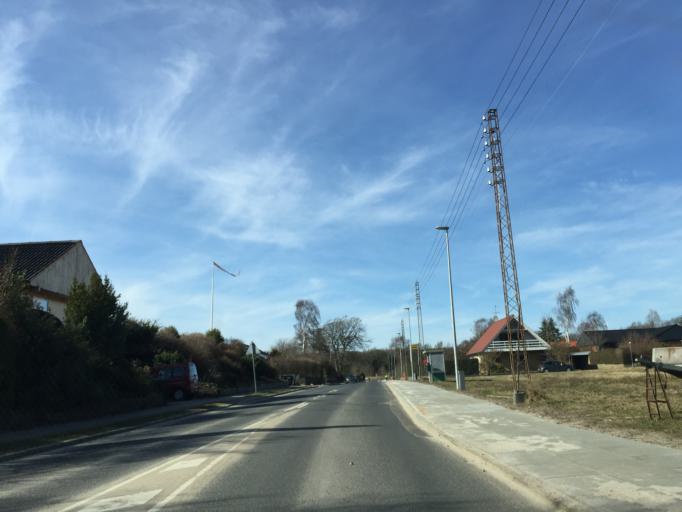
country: DK
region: Central Jutland
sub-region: Silkeborg Kommune
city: Silkeborg
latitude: 56.1934
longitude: 9.5360
